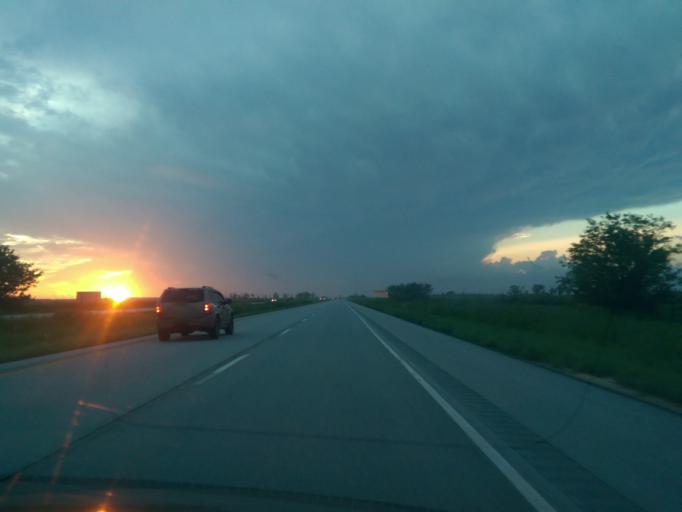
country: US
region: Iowa
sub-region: Fremont County
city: Hamburg
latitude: 40.6096
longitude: -95.6867
